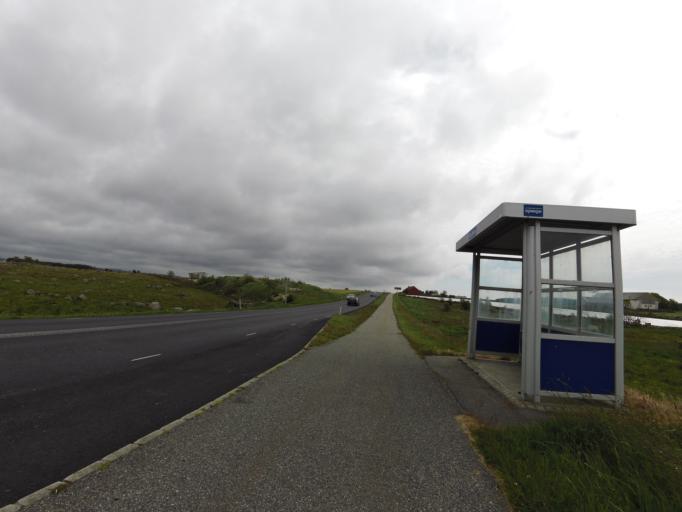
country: NO
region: Rogaland
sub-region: Ha
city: Naerbo
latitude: 58.6413
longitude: 5.6058
